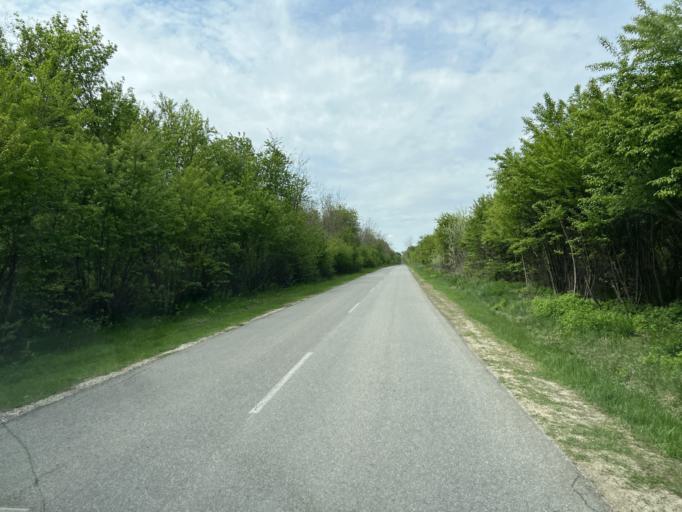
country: HU
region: Pest
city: Csemo
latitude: 47.1434
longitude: 19.6316
